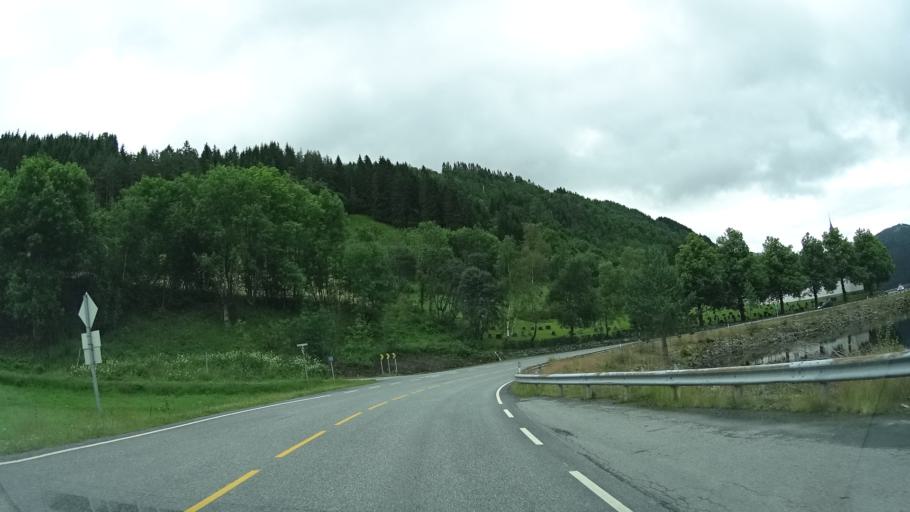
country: NO
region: Hordaland
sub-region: Granvin
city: Granvin
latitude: 60.5566
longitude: 6.7315
